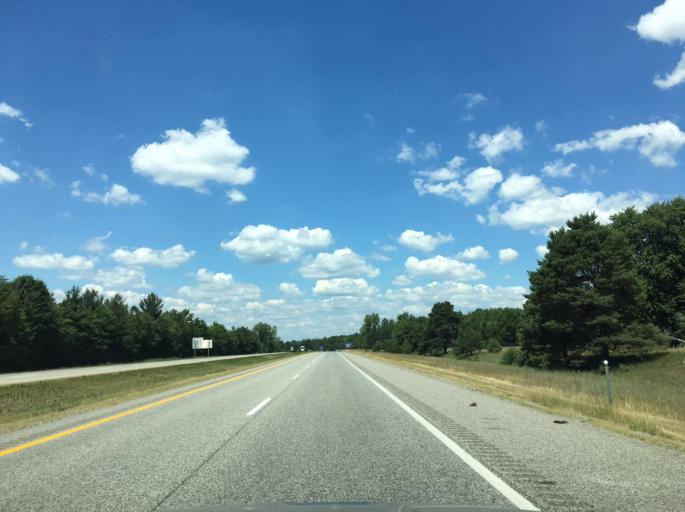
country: US
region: Michigan
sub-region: Midland County
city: Midland
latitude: 43.6518
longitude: -84.2024
